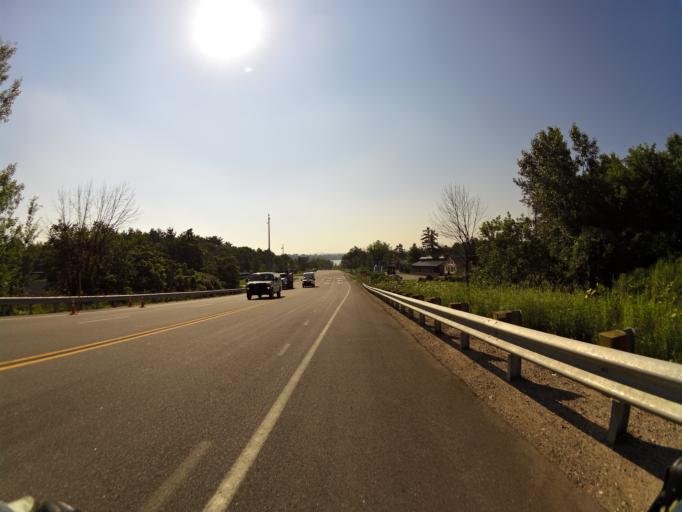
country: CA
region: Quebec
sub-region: Outaouais
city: Gatineau
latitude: 45.4834
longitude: -75.7523
